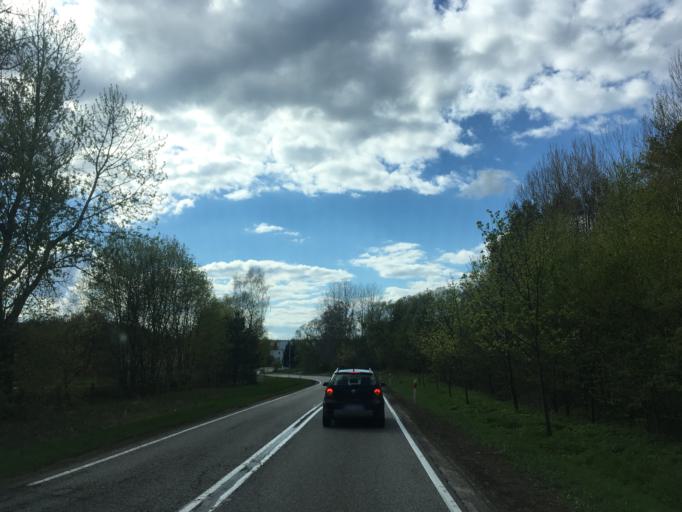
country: PL
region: Warmian-Masurian Voivodeship
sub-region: Powiat szczycienski
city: Szczytno
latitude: 53.5686
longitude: 20.9065
